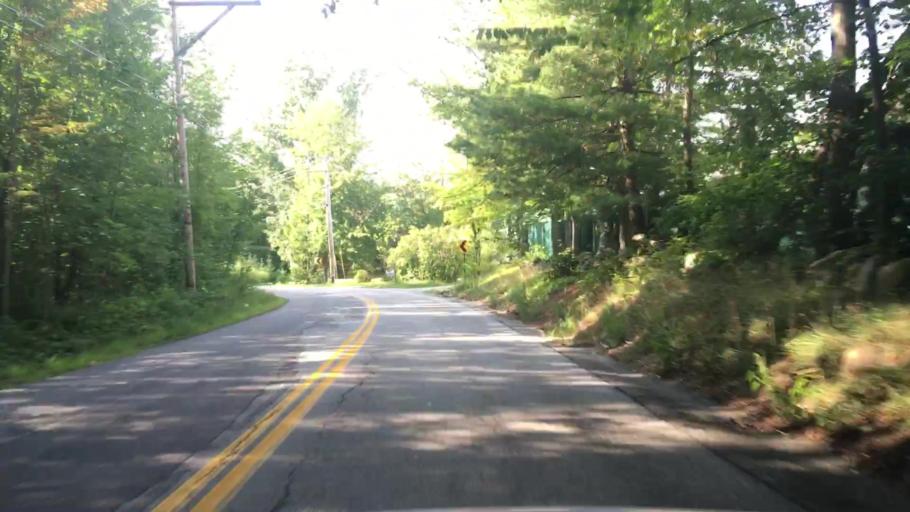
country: US
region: New Hampshire
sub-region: Belknap County
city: Gilford
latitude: 43.5639
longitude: -71.4265
